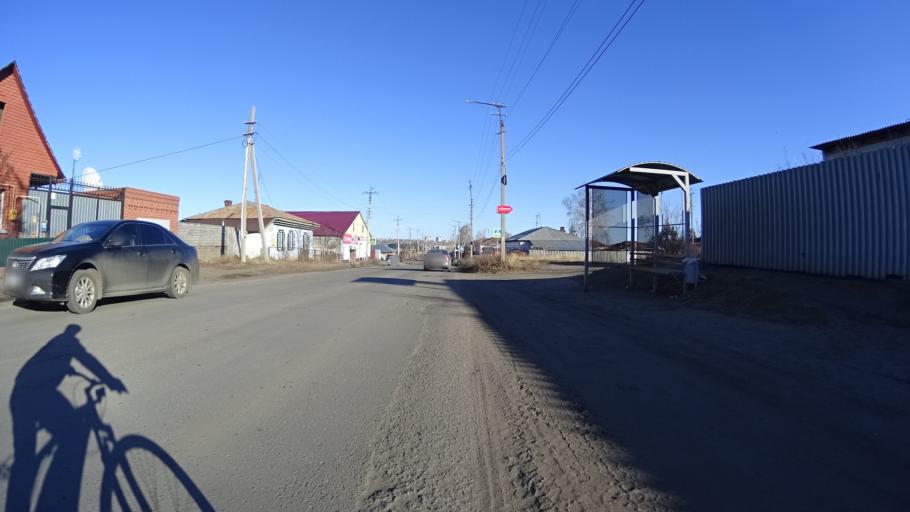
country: RU
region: Chelyabinsk
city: Troitsk
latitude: 54.0873
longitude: 61.5321
